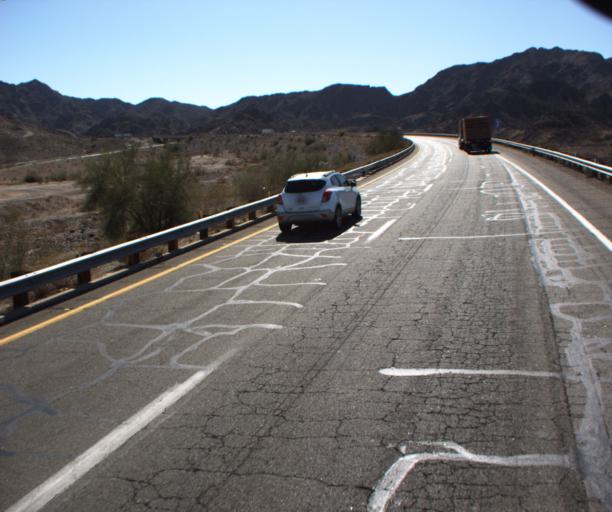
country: US
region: Arizona
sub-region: Yuma County
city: Fortuna Foothills
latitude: 32.6736
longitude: -114.3100
